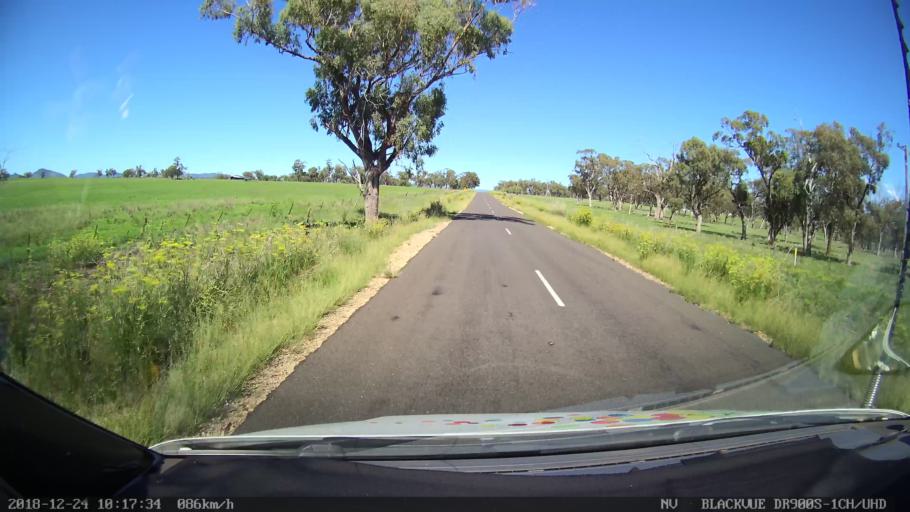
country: AU
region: New South Wales
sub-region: Liverpool Plains
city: Quirindi
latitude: -31.7205
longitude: 150.5893
